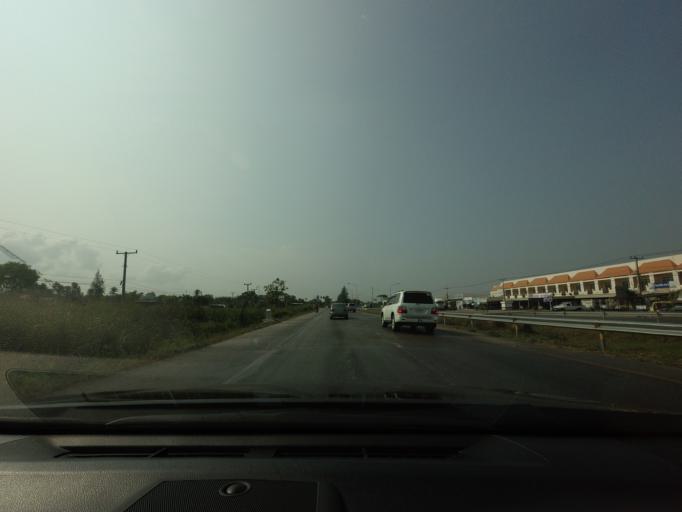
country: TH
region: Prachuap Khiri Khan
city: Pran Buri
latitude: 12.4867
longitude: 99.8911
